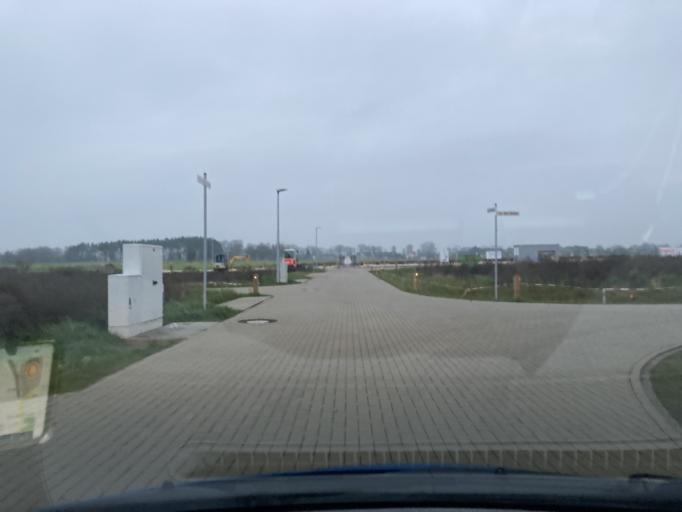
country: DE
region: Lower Saxony
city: Bomlitz
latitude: 52.8714
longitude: 9.6317
